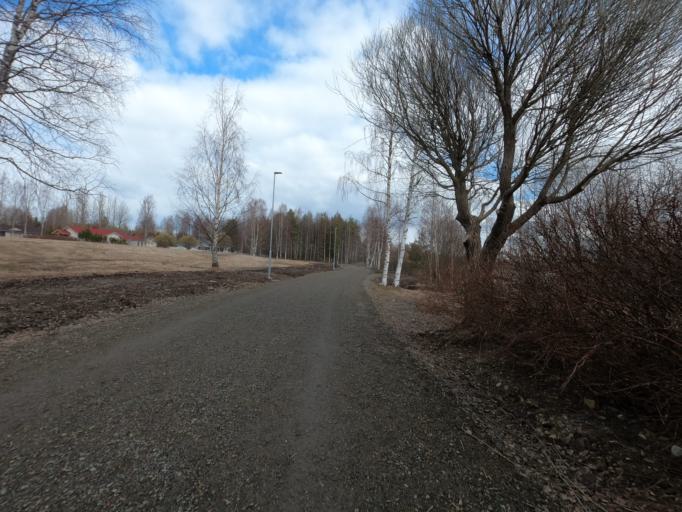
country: FI
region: North Karelia
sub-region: Joensuu
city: Joensuu
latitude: 62.6166
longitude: 29.8600
